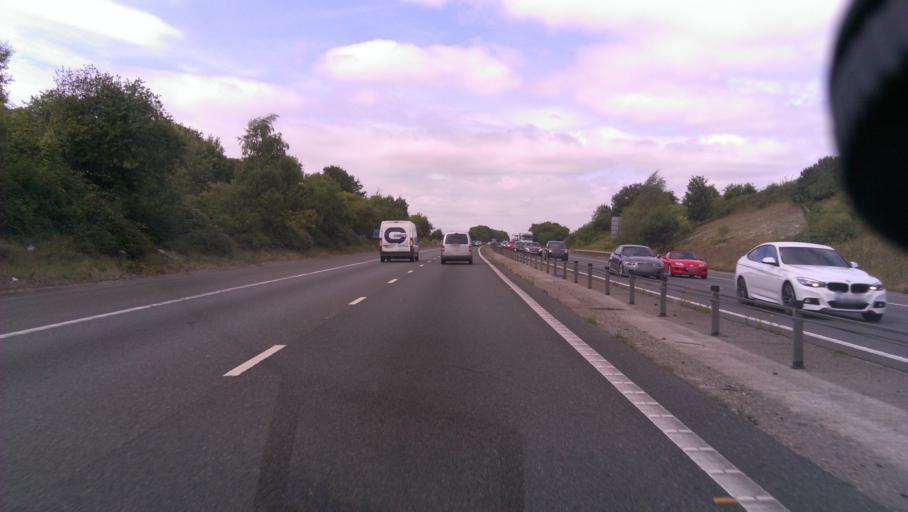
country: GB
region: England
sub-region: Essex
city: Saffron Walden
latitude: 51.9852
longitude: 0.1974
